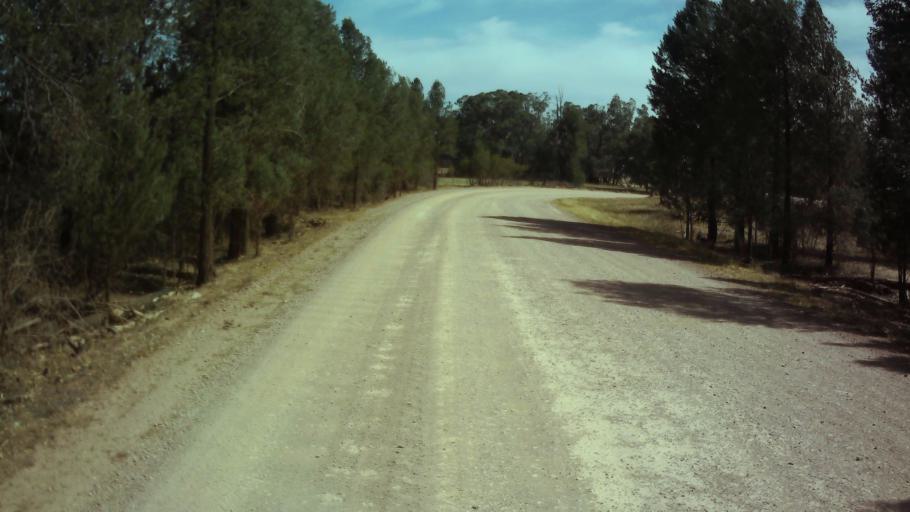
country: AU
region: New South Wales
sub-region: Weddin
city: Grenfell
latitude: -34.0396
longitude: 148.0805
